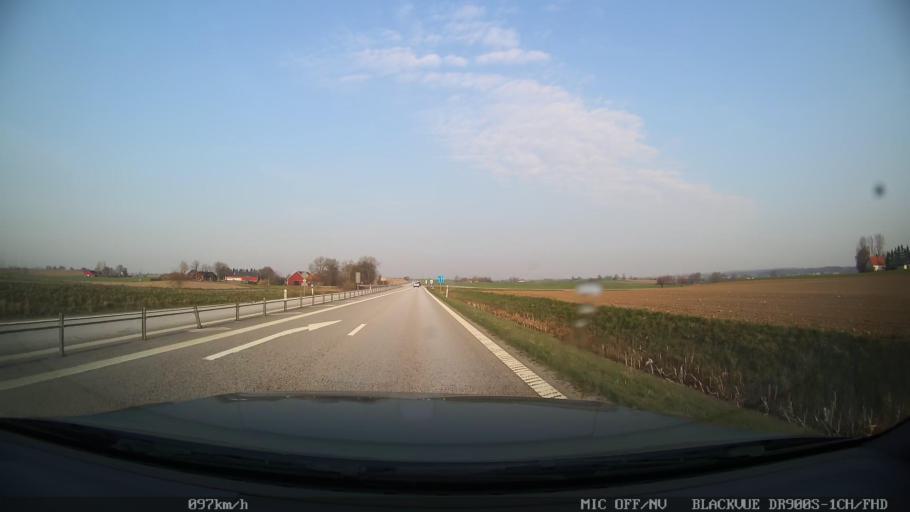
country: SE
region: Skane
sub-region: Skurups Kommun
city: Rydsgard
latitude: 55.4776
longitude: 13.6337
